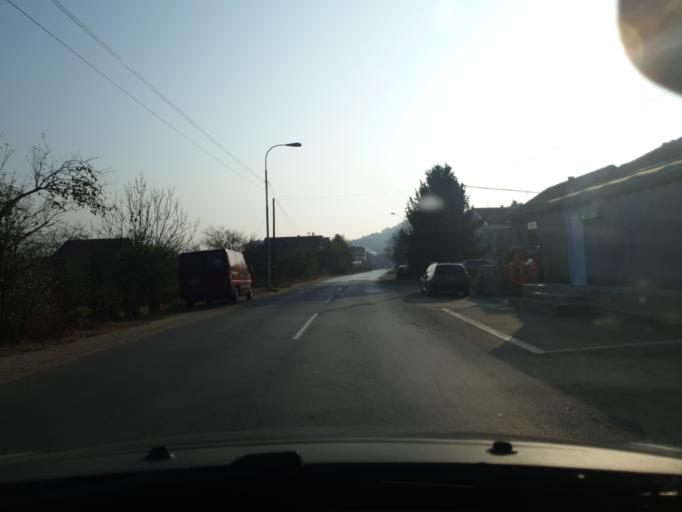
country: RS
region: Central Serbia
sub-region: Jablanicki Okrug
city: Leskovac
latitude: 42.9961
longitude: 21.9274
